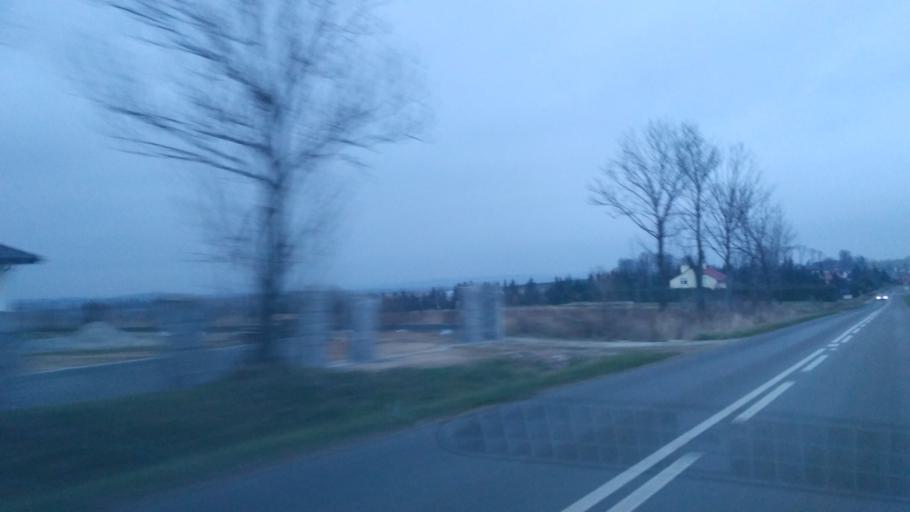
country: PL
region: Subcarpathian Voivodeship
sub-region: Powiat jaroslawski
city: Pruchnik
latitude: 49.9069
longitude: 22.5014
